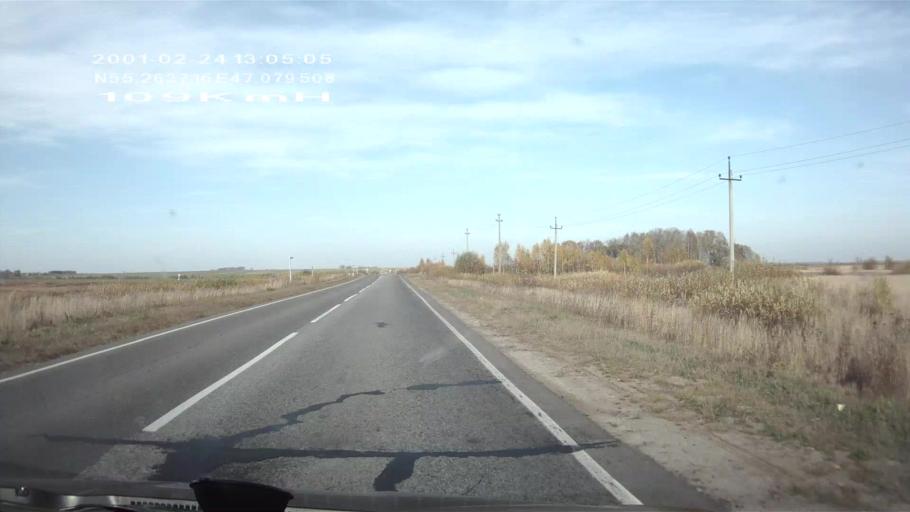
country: RU
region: Chuvashia
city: Ibresi
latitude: 55.2639
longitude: 47.0795
